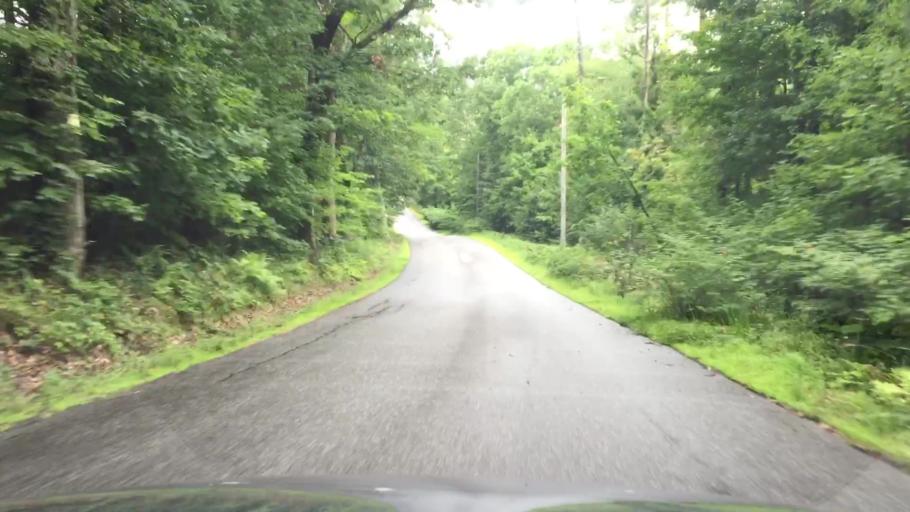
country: US
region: New Hampshire
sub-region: Carroll County
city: Center Harbor
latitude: 43.7176
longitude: -71.4812
